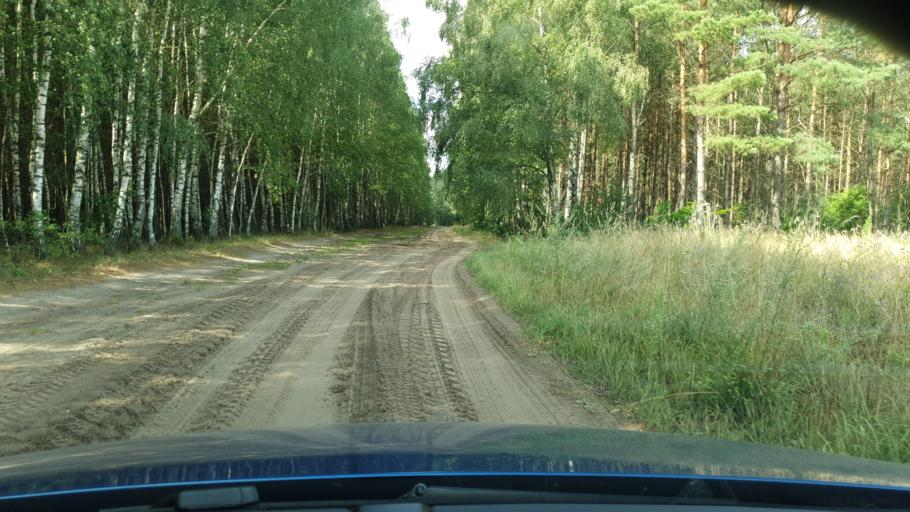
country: PL
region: Pomeranian Voivodeship
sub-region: Powiat czluchowski
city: Przechlewo
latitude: 53.8058
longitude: 17.3668
